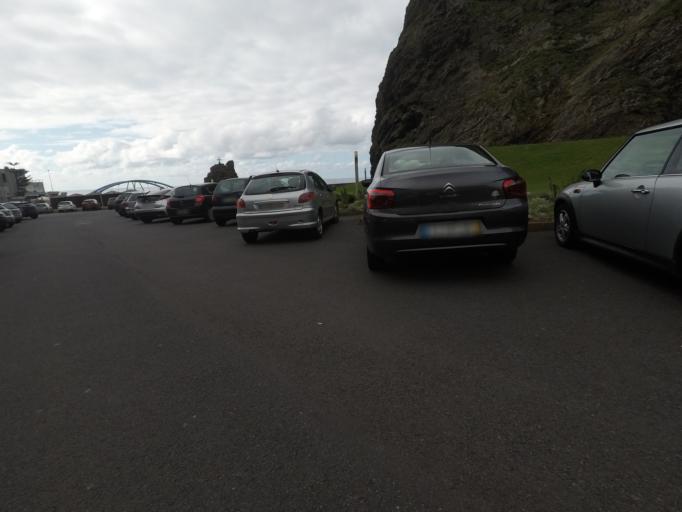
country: PT
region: Madeira
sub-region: Sao Vicente
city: Sao Vicente
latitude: 32.8078
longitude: -17.0476
